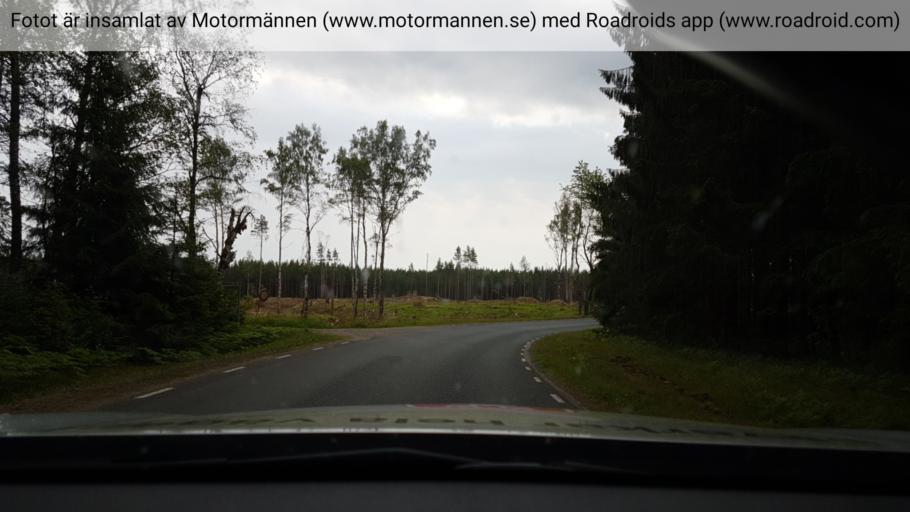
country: SE
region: Joenkoeping
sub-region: Habo Kommun
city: Habo
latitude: 58.0100
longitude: 14.0083
